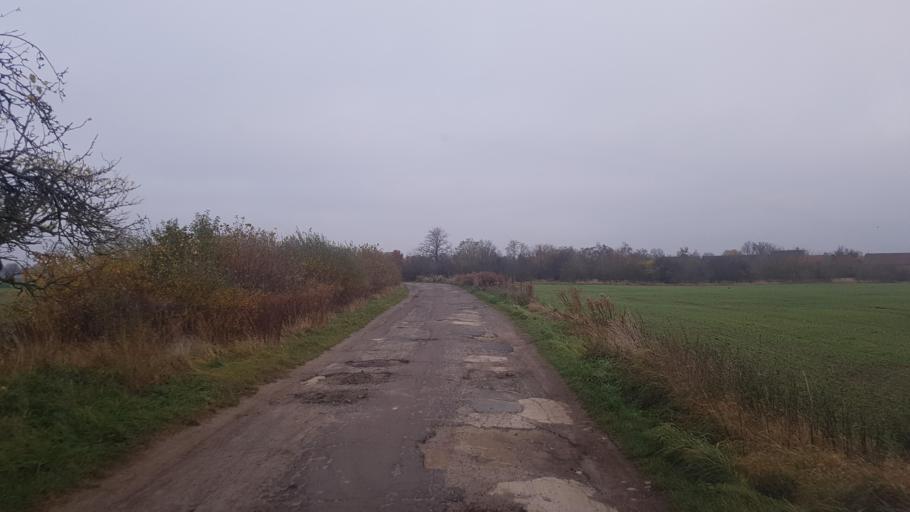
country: DE
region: Brandenburg
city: Gross Kreutz
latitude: 52.3667
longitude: 12.8245
